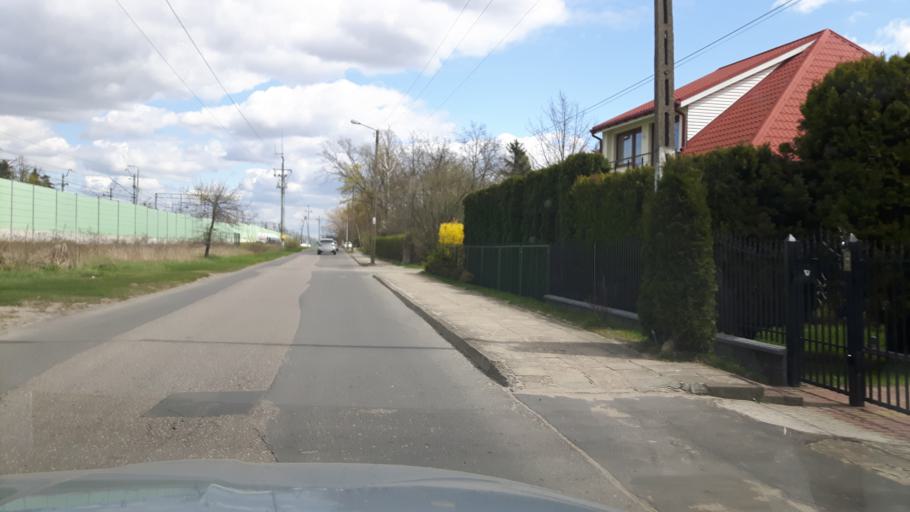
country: PL
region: Masovian Voivodeship
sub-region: Powiat wolominski
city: Wolomin
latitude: 52.3399
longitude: 21.2236
